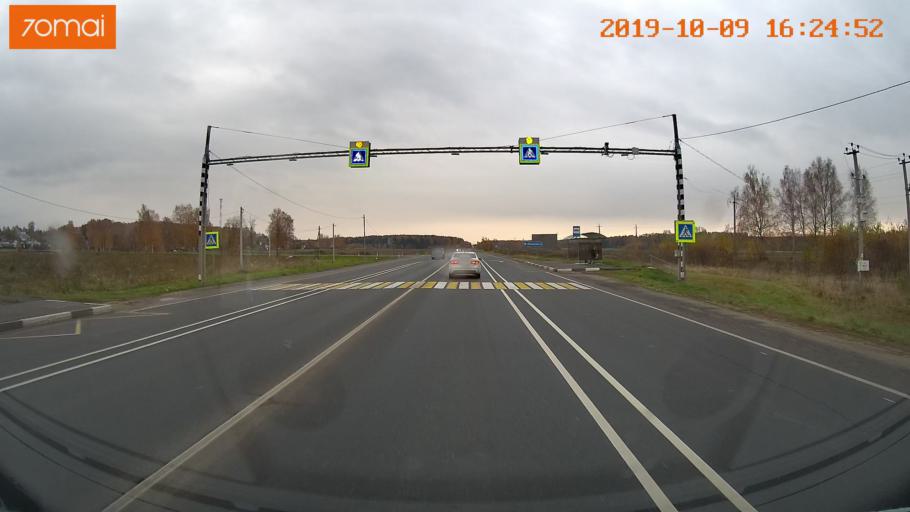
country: RU
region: Kostroma
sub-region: Kostromskoy Rayon
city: Kostroma
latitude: 57.6478
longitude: 40.9147
